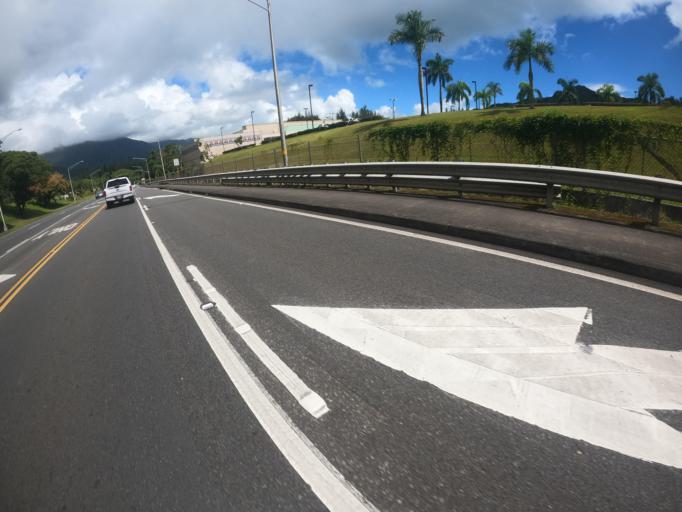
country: US
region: Hawaii
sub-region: Honolulu County
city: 'Ahuimanu
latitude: 21.4358
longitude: -157.8264
